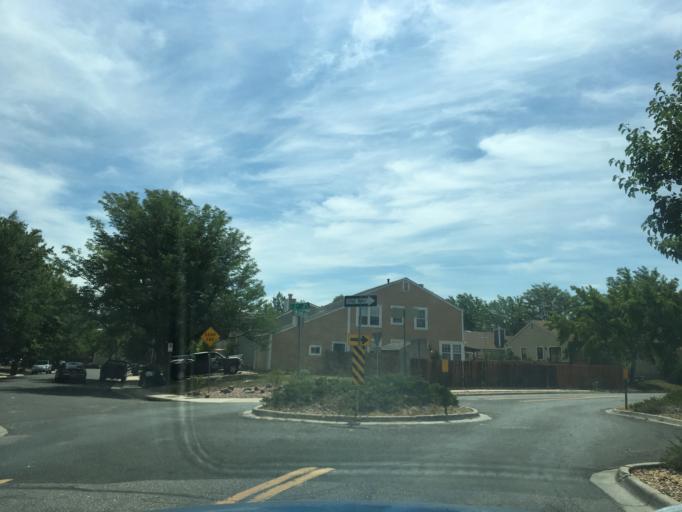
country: US
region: Colorado
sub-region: Adams County
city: Aurora
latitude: 39.7179
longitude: -104.8570
